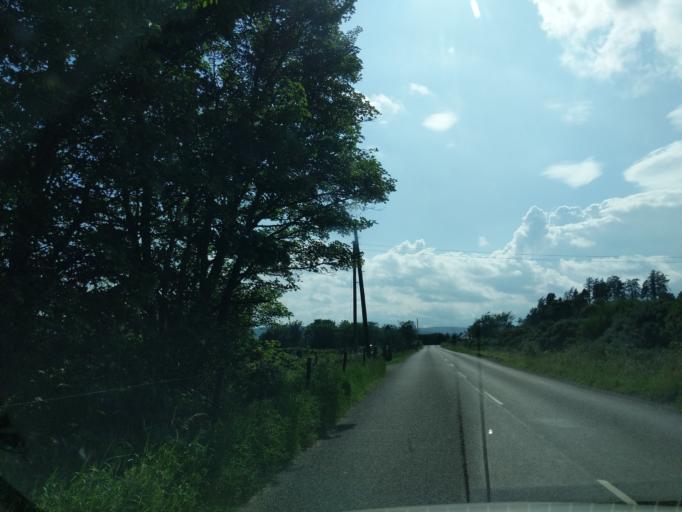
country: GB
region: Scotland
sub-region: Moray
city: Rothes
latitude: 57.5450
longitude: -3.1729
